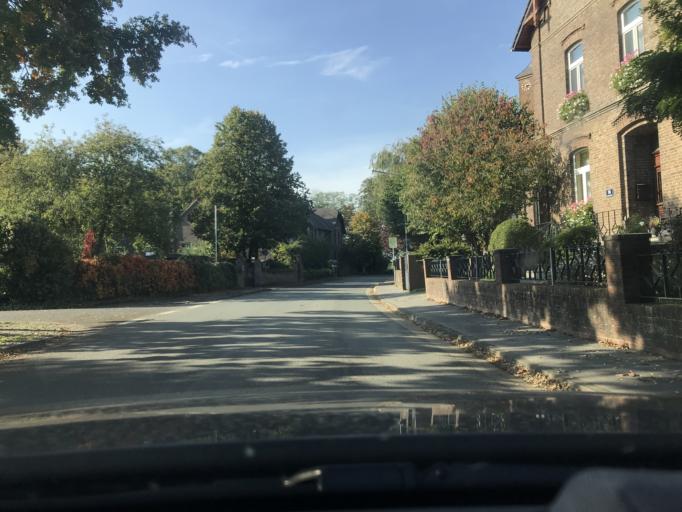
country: DE
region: North Rhine-Westphalia
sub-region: Regierungsbezirk Dusseldorf
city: Emmerich
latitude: 51.7898
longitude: 6.2329
